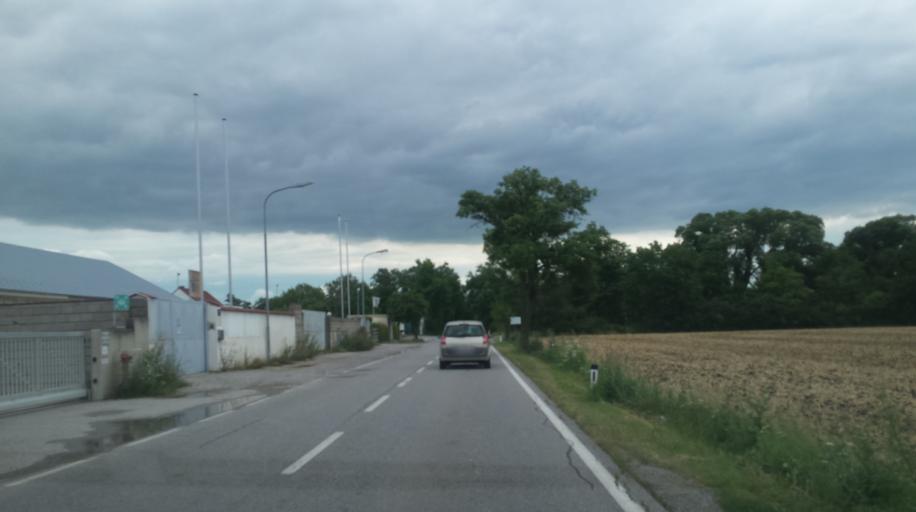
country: AT
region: Lower Austria
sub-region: Politischer Bezirk Wien-Umgebung
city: Zwolfaxing
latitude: 48.1155
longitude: 16.4575
